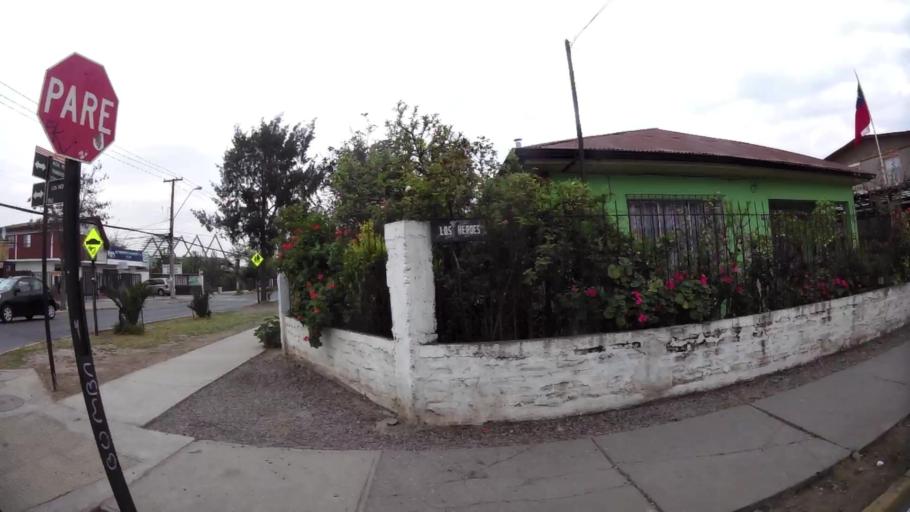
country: CL
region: Santiago Metropolitan
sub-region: Provincia de Santiago
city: Lo Prado
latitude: -33.5022
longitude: -70.7521
